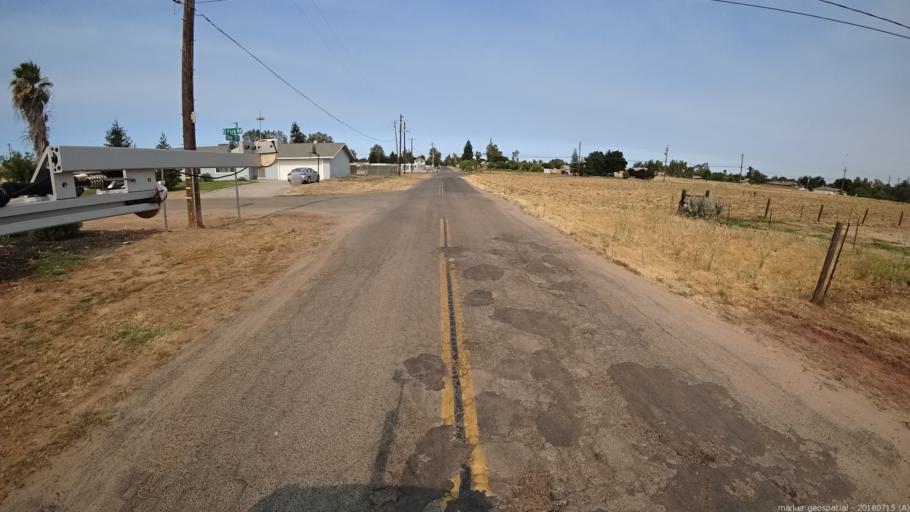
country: US
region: California
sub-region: Madera County
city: Madera Acres
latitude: 37.0036
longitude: -120.0729
